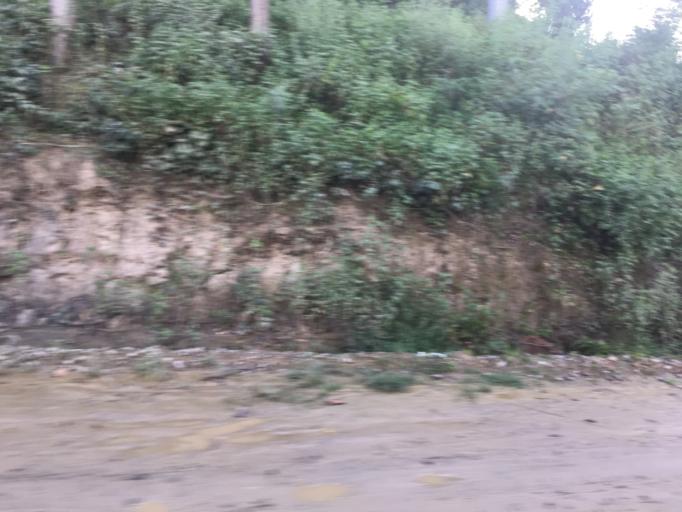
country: NP
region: Central Region
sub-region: Bagmati Zone
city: Bhaktapur
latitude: 27.6942
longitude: 85.4613
